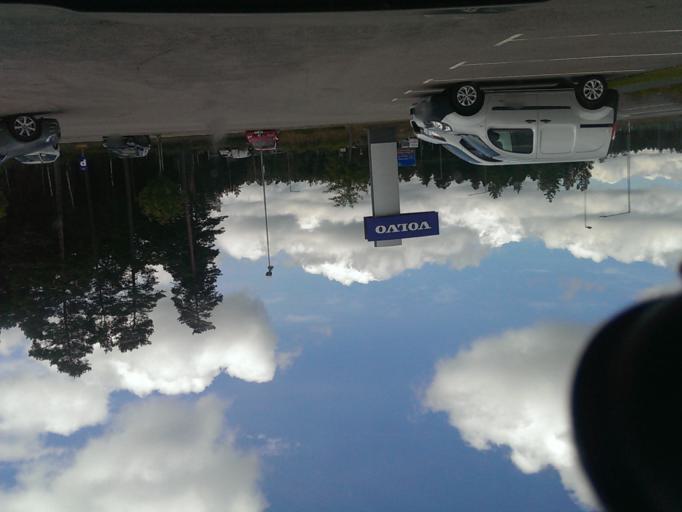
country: SE
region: Joenkoeping
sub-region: Varnamo Kommun
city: Varnamo
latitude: 57.1918
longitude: 14.0641
